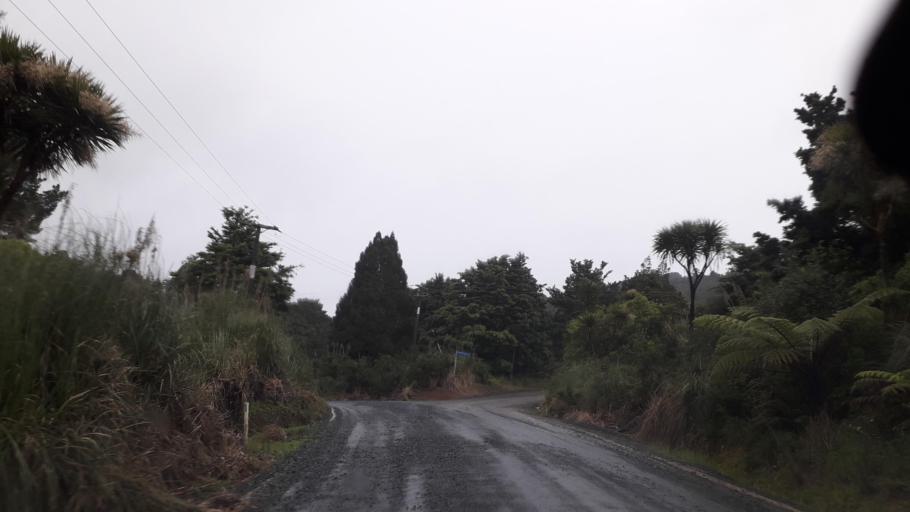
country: NZ
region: Northland
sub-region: Far North District
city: Kerikeri
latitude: -35.1177
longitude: 173.7509
